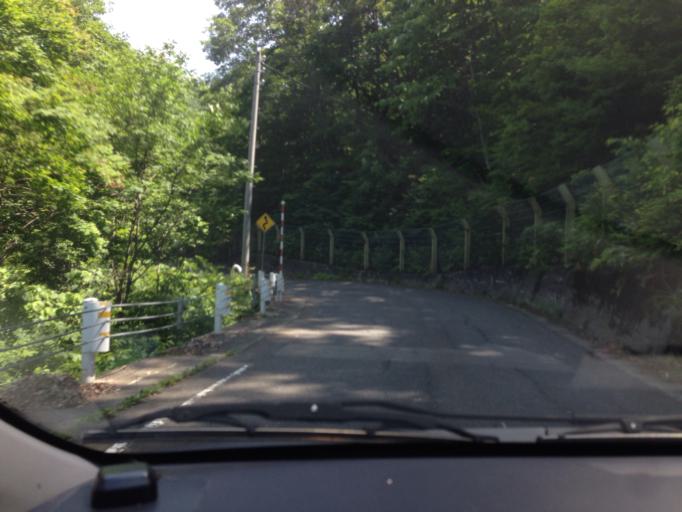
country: JP
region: Fukushima
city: Kitakata
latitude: 37.2814
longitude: 139.6855
